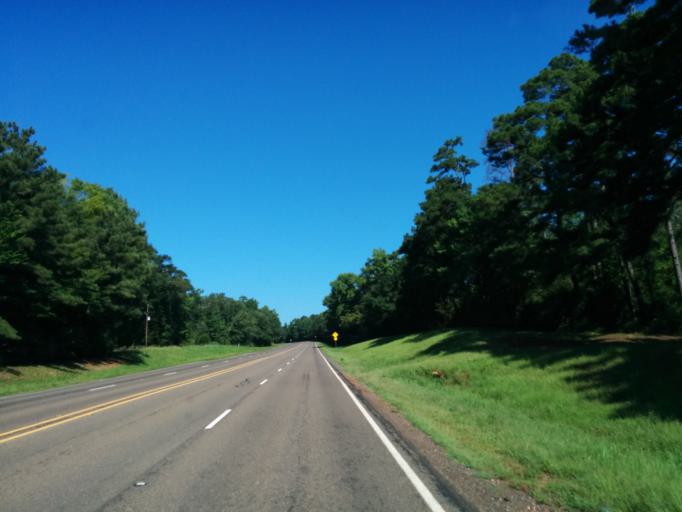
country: US
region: Texas
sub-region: Sabine County
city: Milam
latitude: 31.4329
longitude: -93.8355
